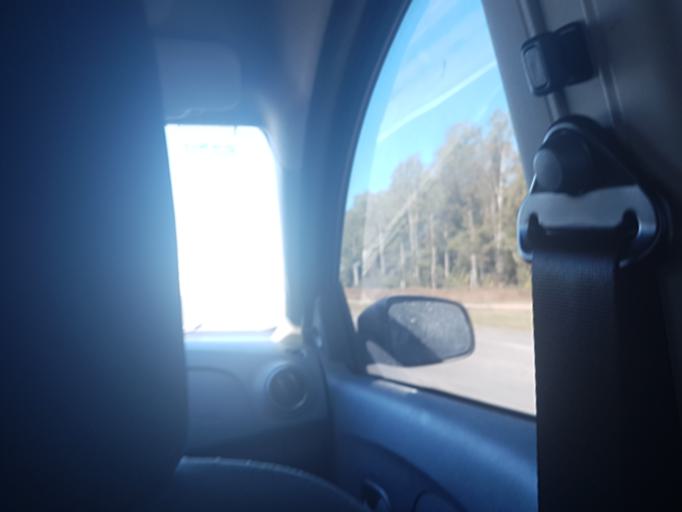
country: AR
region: Cordoba
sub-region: Departamento de Rio Segundo
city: Rio Segundo
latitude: -31.6326
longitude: -63.8735
